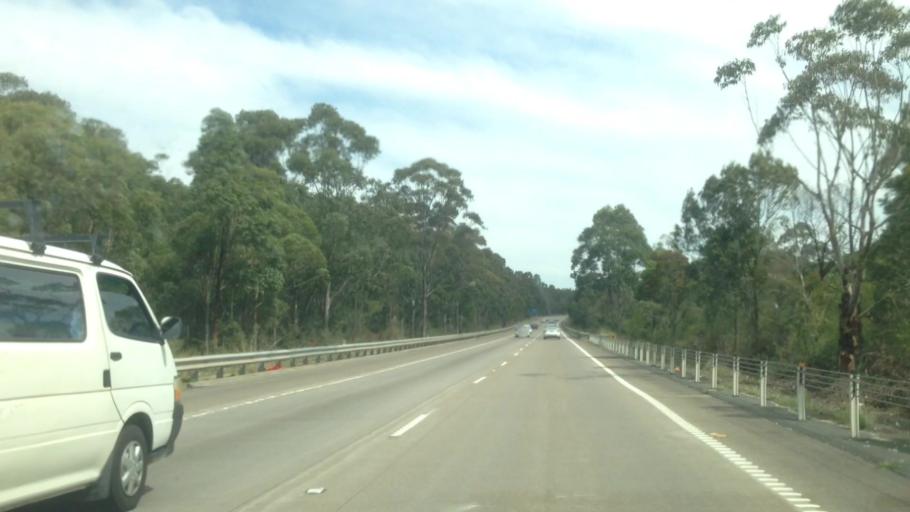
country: AU
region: New South Wales
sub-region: Lake Macquarie Shire
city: Fennell Bay
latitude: -32.9704
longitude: 151.5344
